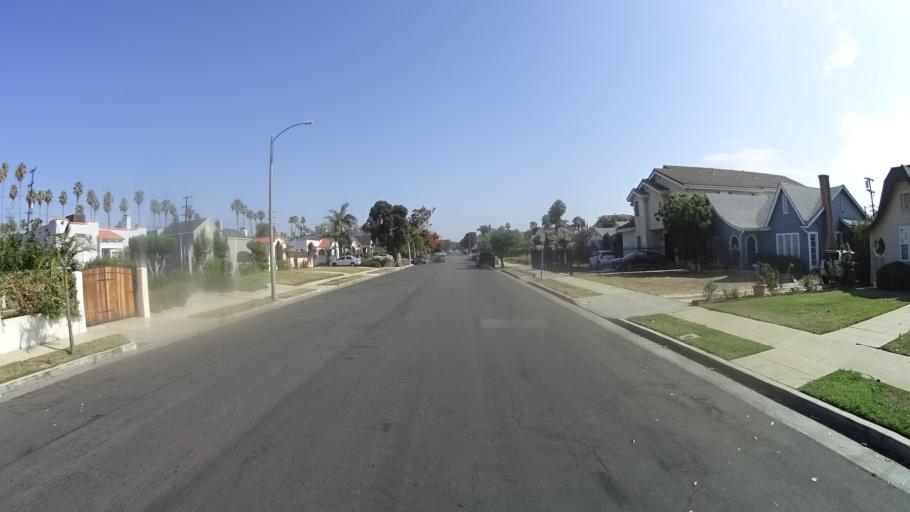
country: US
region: California
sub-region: Los Angeles County
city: View Park-Windsor Hills
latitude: 33.9917
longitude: -118.3366
